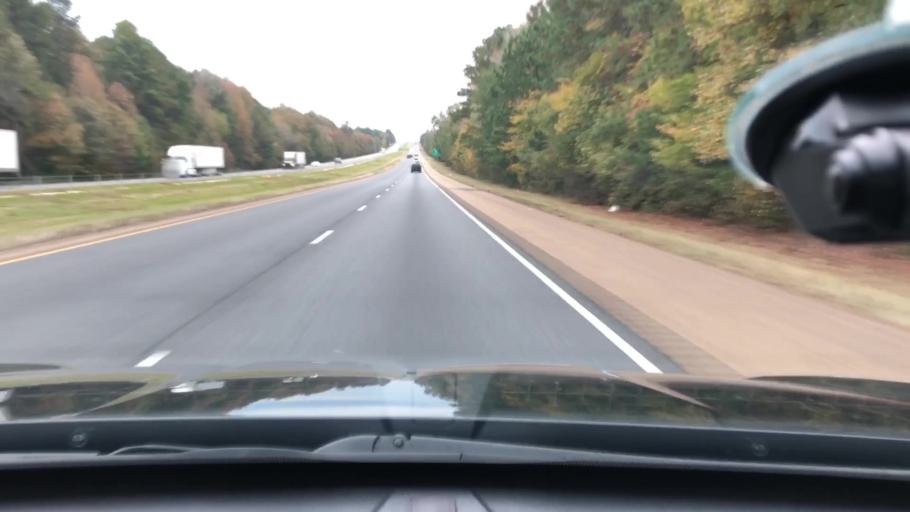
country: US
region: Arkansas
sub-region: Clark County
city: Gurdon
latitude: 33.9801
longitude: -93.2003
